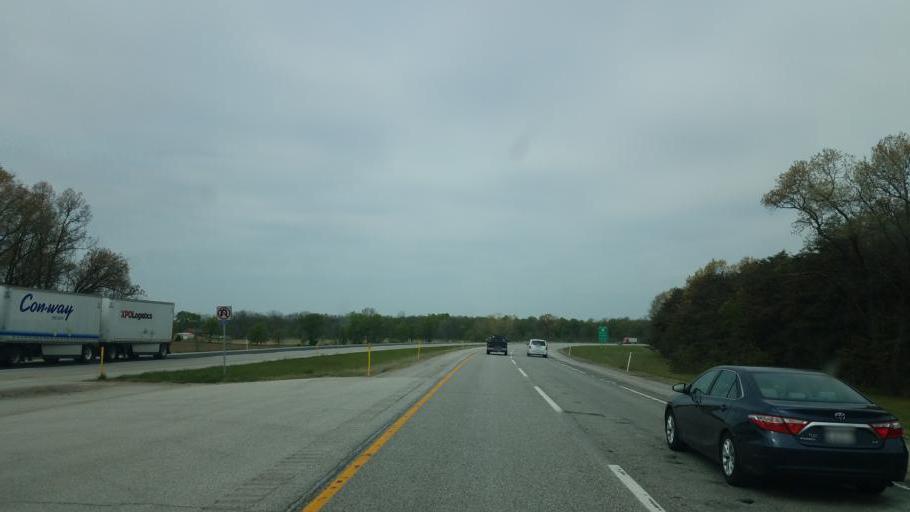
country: US
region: Indiana
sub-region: Elkhart County
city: Bristol
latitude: 41.7295
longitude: -85.7652
